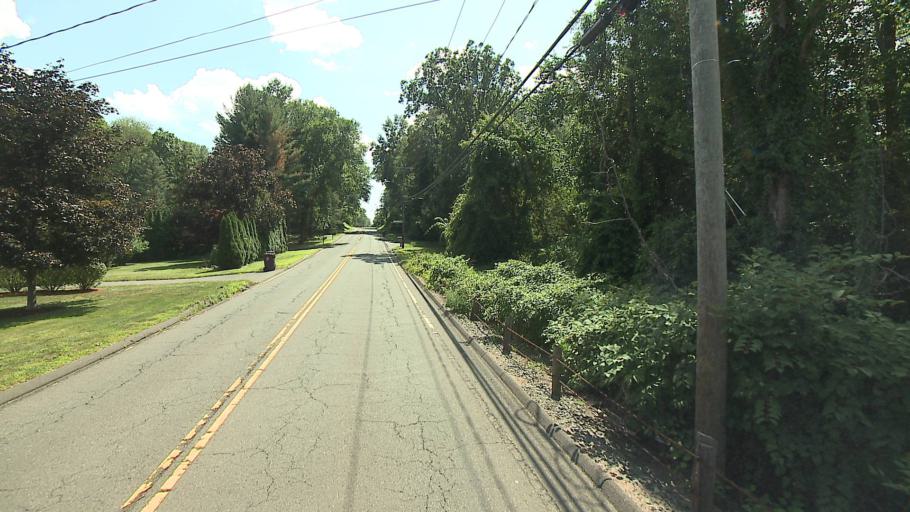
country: US
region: Connecticut
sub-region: Hartford County
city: Farmington
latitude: 41.7213
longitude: -72.8054
